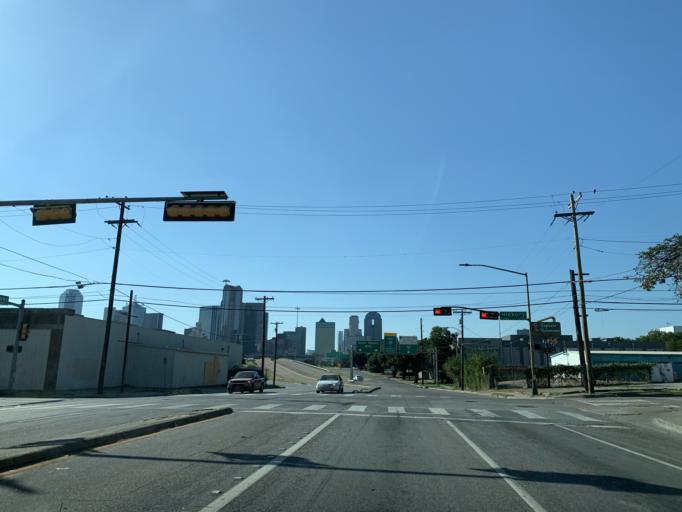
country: US
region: Texas
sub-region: Dallas County
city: Dallas
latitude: 32.7731
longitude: -96.7828
